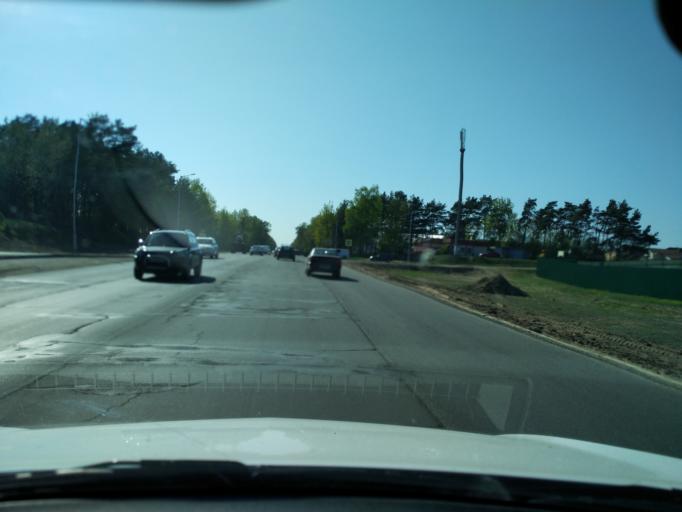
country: BY
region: Minsk
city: Borovlyany
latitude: 53.9651
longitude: 27.6665
